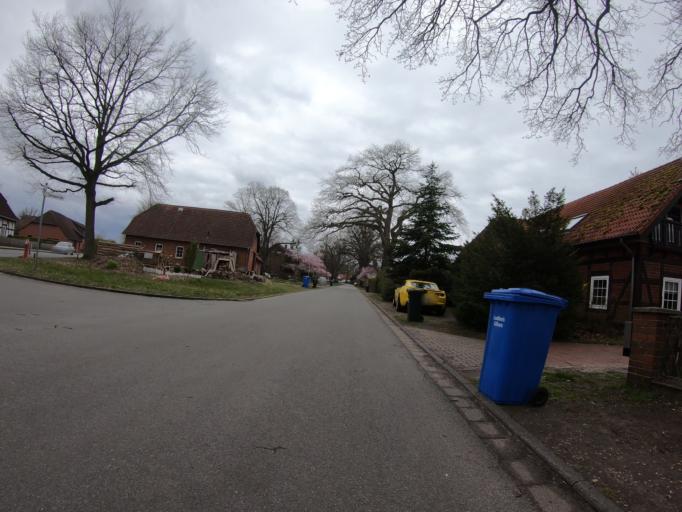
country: DE
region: Lower Saxony
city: Muden
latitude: 52.5000
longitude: 10.4140
